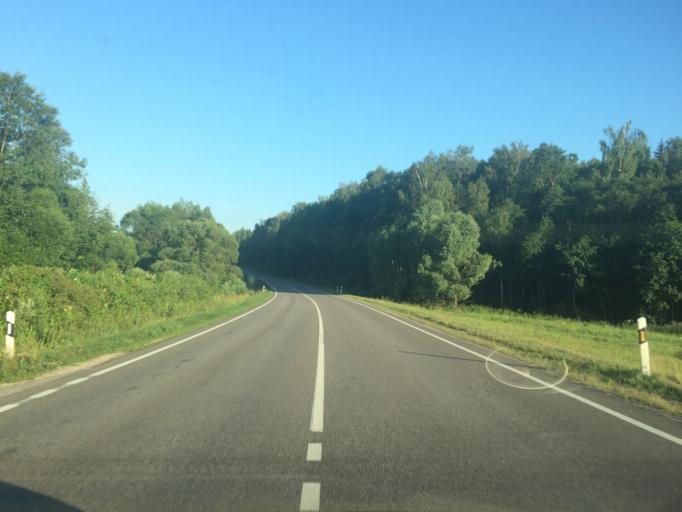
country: LT
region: Utenos apskritis
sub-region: Anyksciai
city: Anyksciai
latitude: 55.4038
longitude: 25.1330
